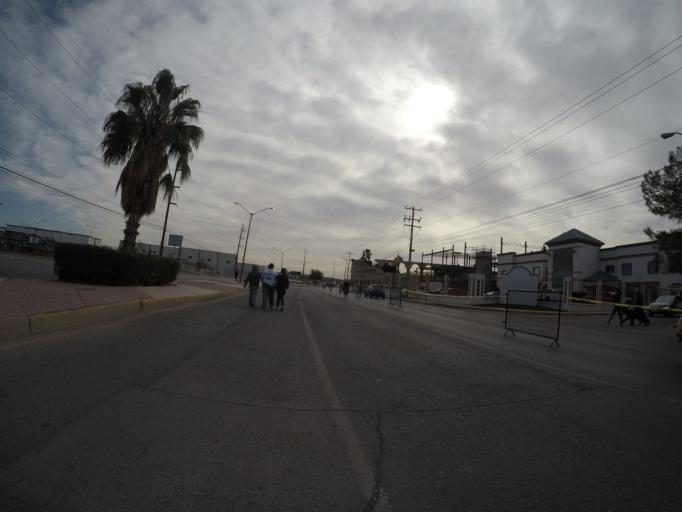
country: MX
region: Chihuahua
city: Ciudad Juarez
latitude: 31.7242
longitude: -106.4013
